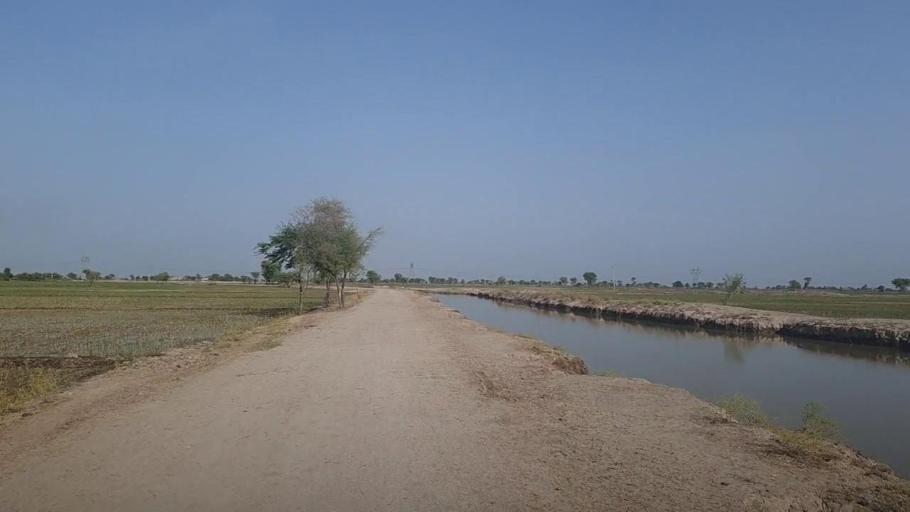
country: PK
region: Sindh
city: Sita Road
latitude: 27.0911
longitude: 67.8489
